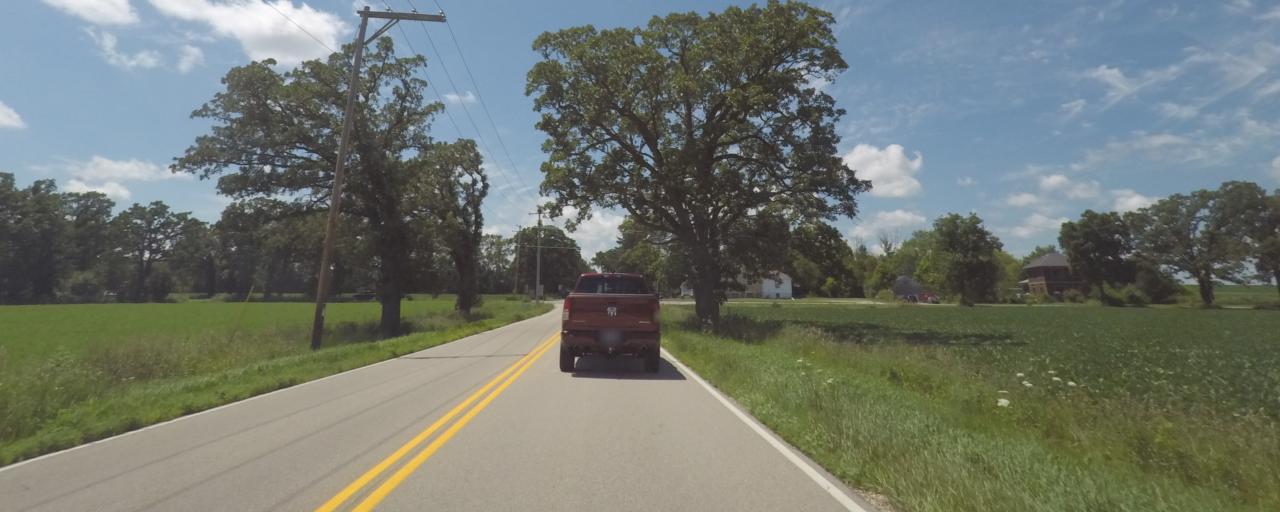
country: US
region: Wisconsin
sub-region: Jefferson County
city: Palmyra
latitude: 42.9273
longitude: -88.5406
